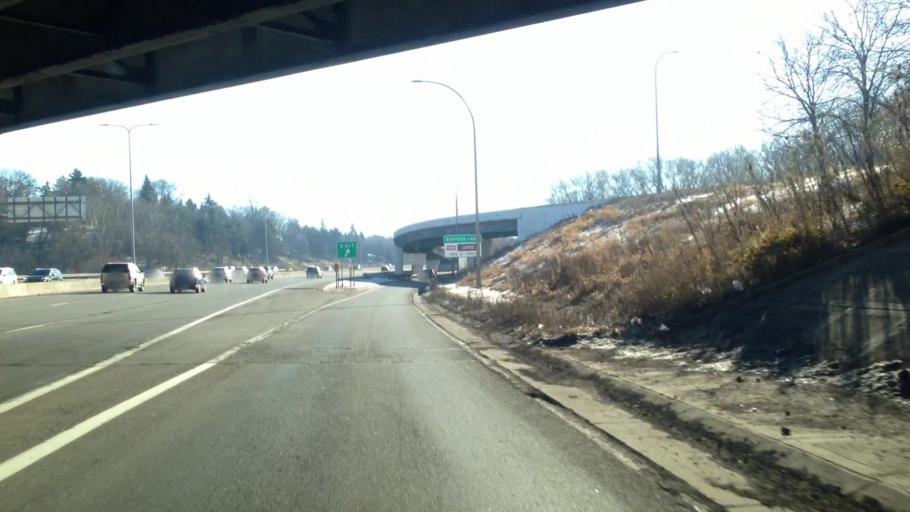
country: US
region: Minnesota
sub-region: Hennepin County
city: Saint Louis Park
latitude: 44.9774
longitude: -93.3447
